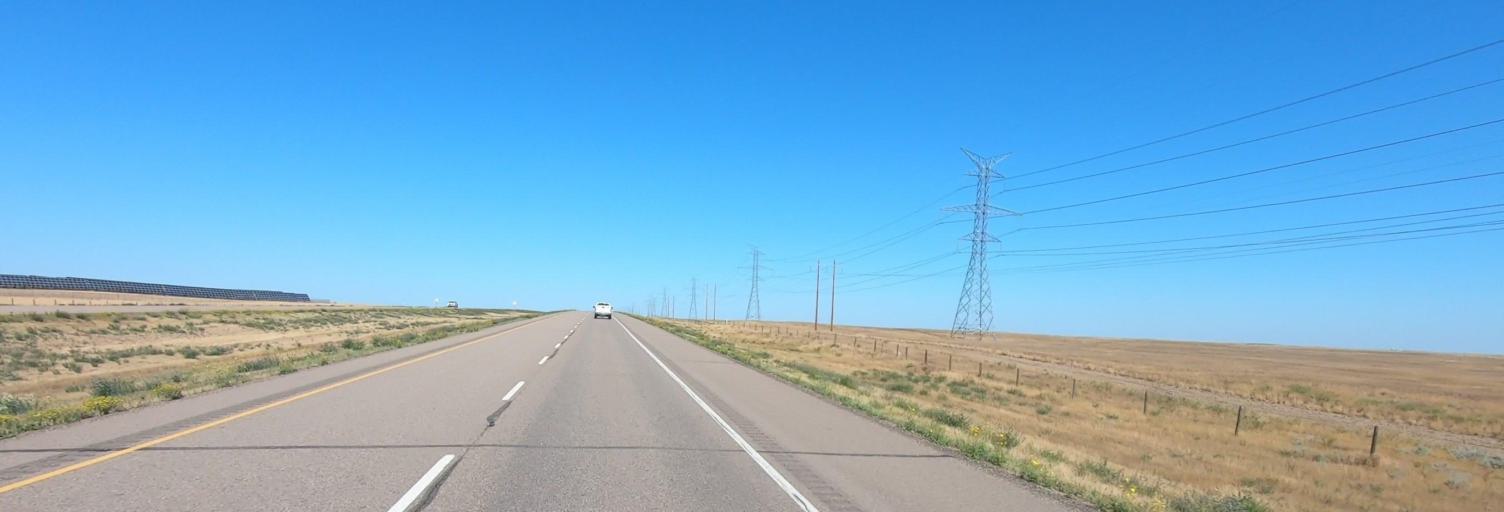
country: CA
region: Alberta
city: Bow Island
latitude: 50.2722
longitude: -111.2672
